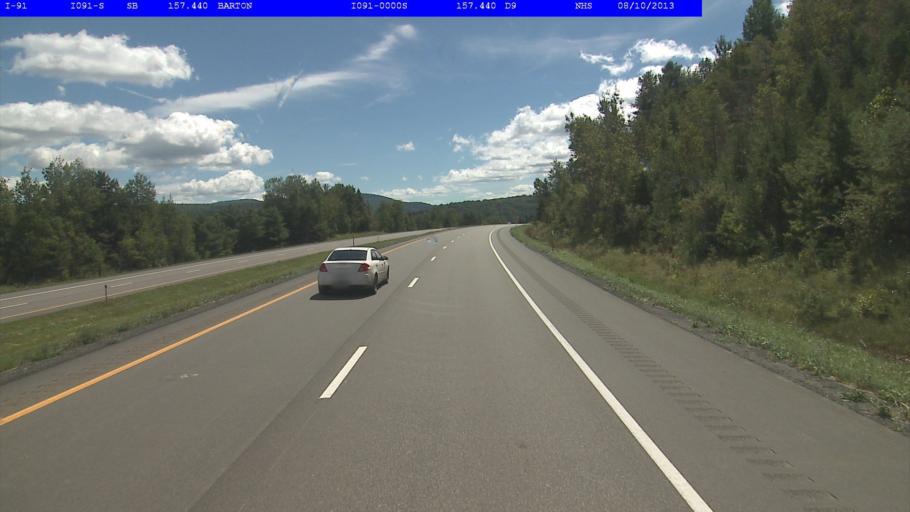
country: US
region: Vermont
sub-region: Orleans County
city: Newport
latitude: 44.7543
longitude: -72.1966
